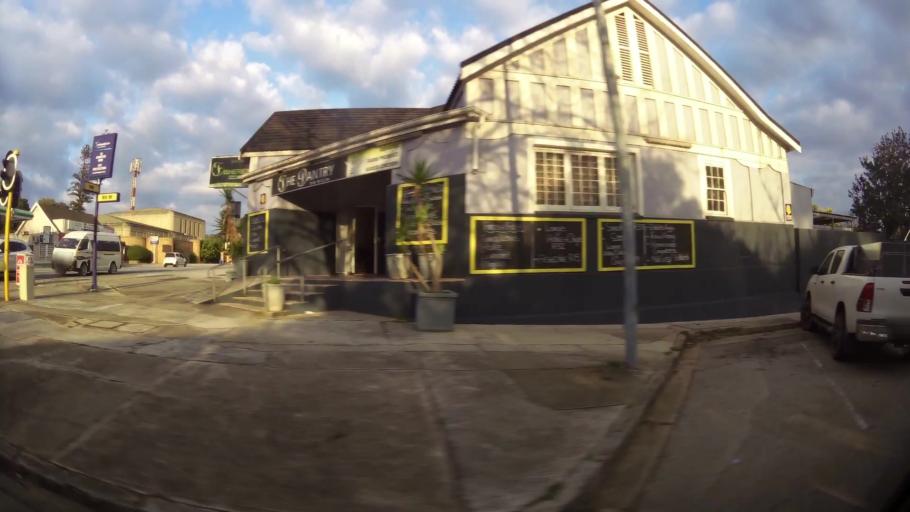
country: ZA
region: Eastern Cape
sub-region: Nelson Mandela Bay Metropolitan Municipality
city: Port Elizabeth
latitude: -33.9803
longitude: 25.5799
